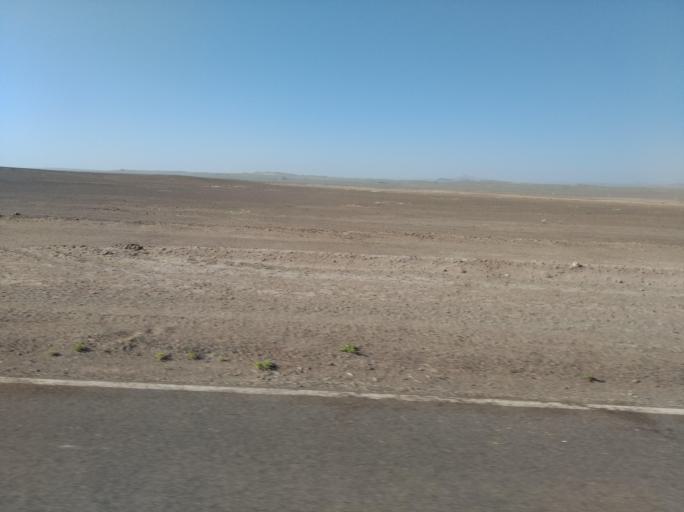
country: CL
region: Atacama
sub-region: Provincia de Copiapo
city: Copiapo
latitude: -27.3237
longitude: -70.8089
